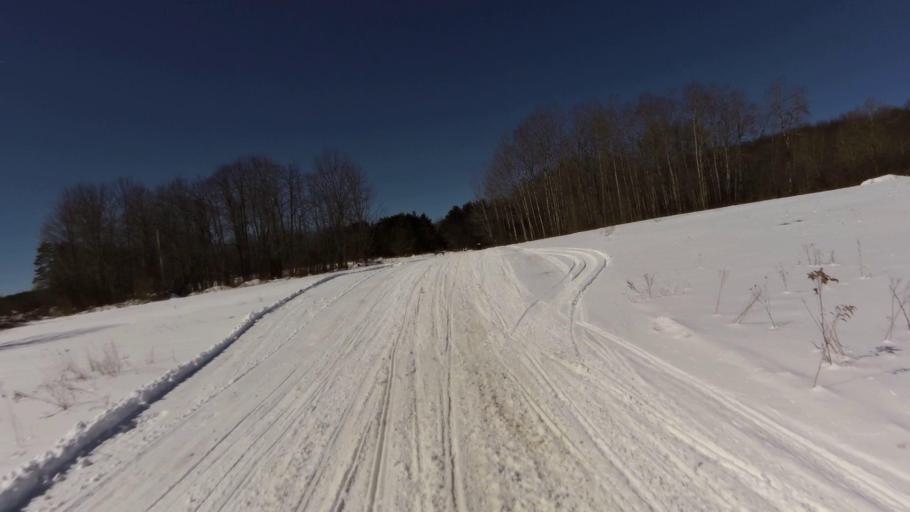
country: US
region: New York
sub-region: Allegany County
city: Houghton
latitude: 42.4002
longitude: -78.2655
